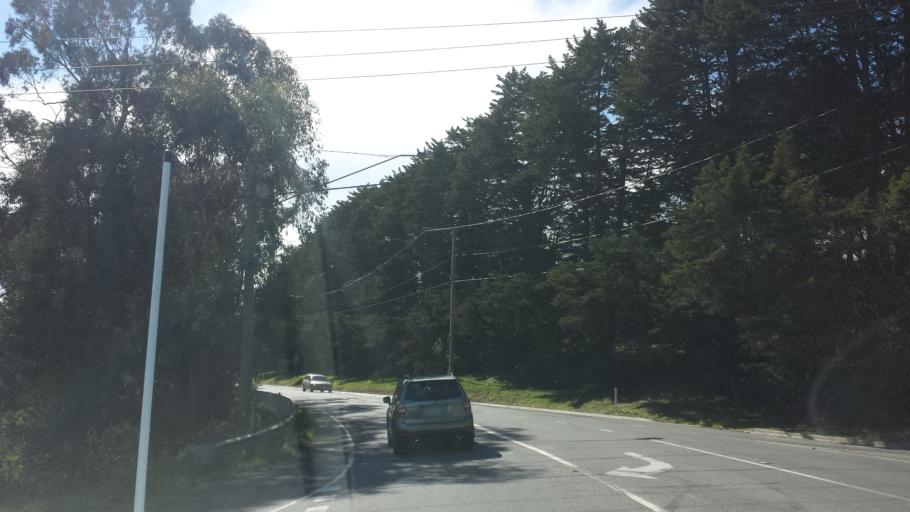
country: AU
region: Victoria
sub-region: Manningham
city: Park Orchards
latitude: -37.7693
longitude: 145.2303
